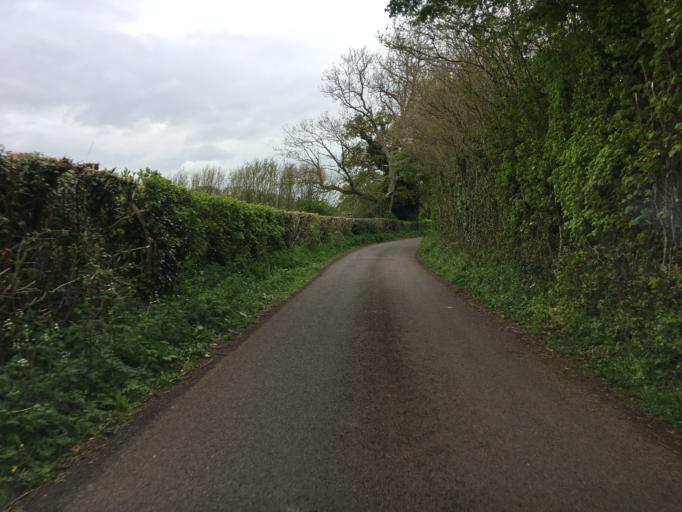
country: GB
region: England
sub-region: Bath and North East Somerset
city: Clutton
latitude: 51.3393
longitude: -2.5329
